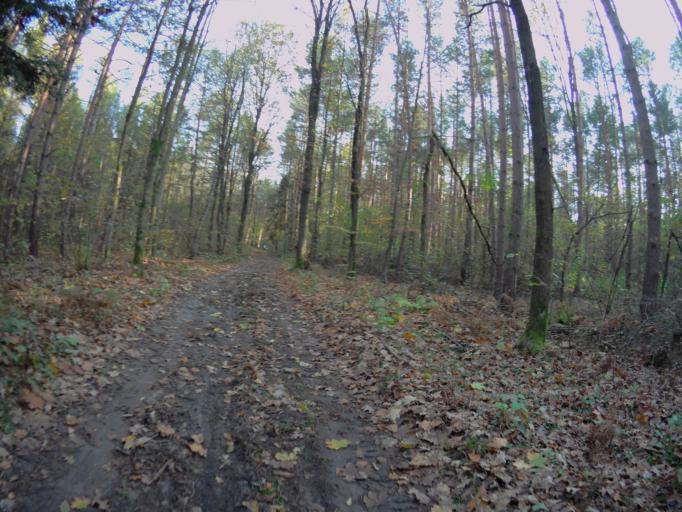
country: PL
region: Subcarpathian Voivodeship
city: Nowa Sarzyna
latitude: 50.3101
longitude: 22.3488
